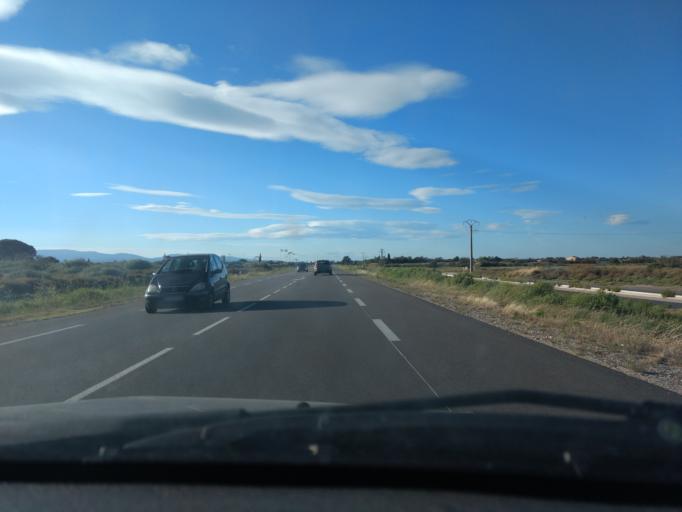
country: FR
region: Languedoc-Roussillon
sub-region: Departement des Pyrenees-Orientales
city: Torreilles
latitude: 42.7552
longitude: 3.0209
